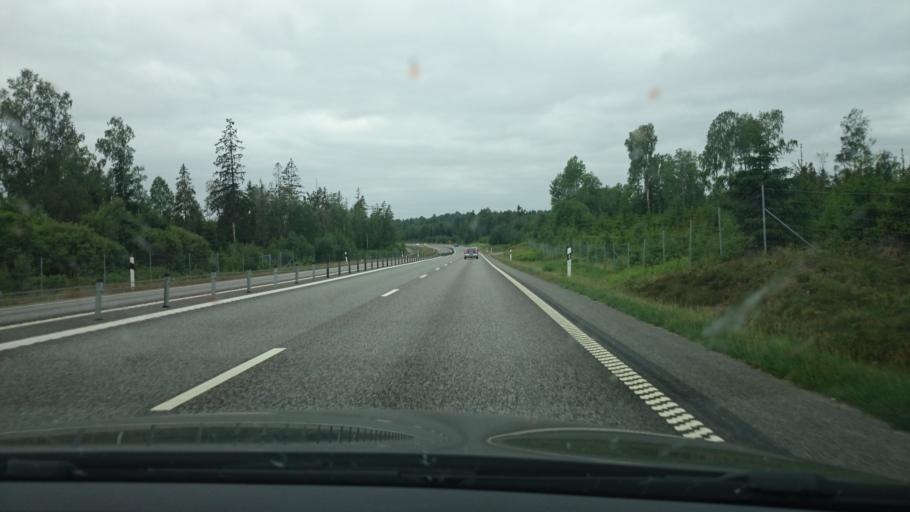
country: SE
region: Halland
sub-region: Hylte Kommun
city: Hyltebruk
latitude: 56.9775
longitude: 13.1915
